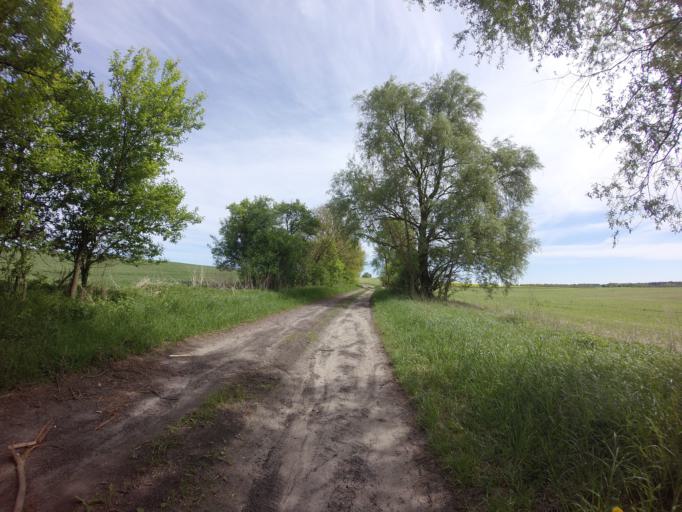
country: PL
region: West Pomeranian Voivodeship
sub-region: Powiat choszczenski
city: Recz
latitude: 53.1720
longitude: 15.5655
